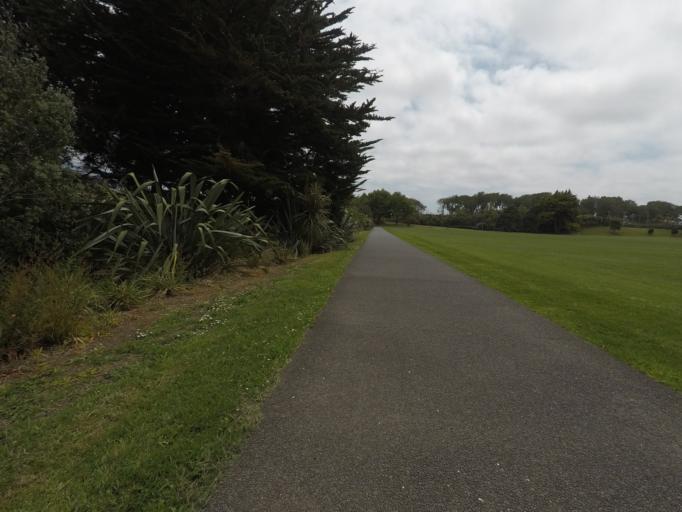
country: NZ
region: Auckland
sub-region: Auckland
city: Auckland
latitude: -36.9147
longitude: 174.7423
